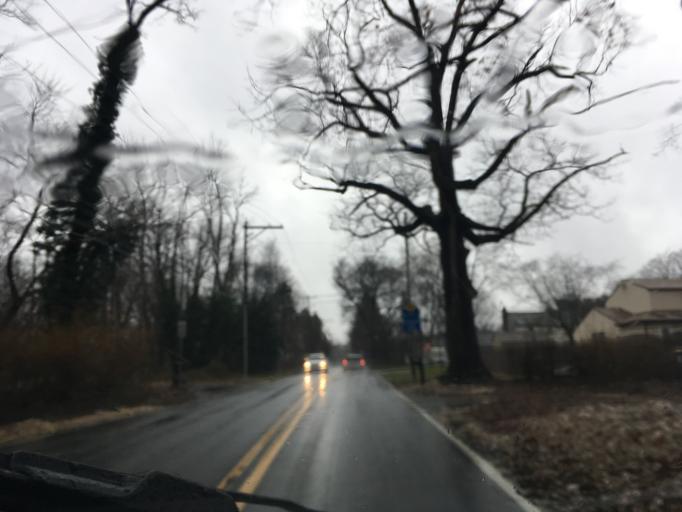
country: US
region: Delaware
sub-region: New Castle County
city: Bellefonte
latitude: 39.8191
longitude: -75.5142
